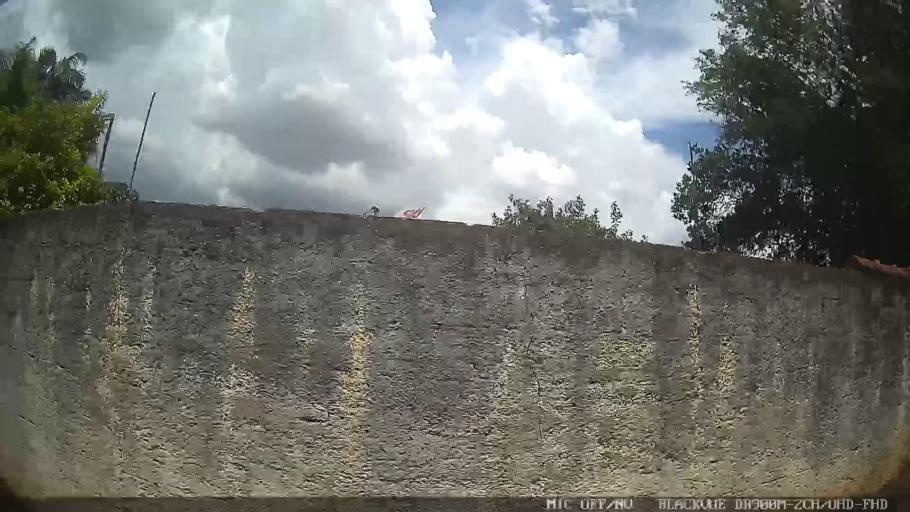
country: BR
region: Sao Paulo
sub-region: Atibaia
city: Atibaia
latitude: -23.1214
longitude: -46.5945
